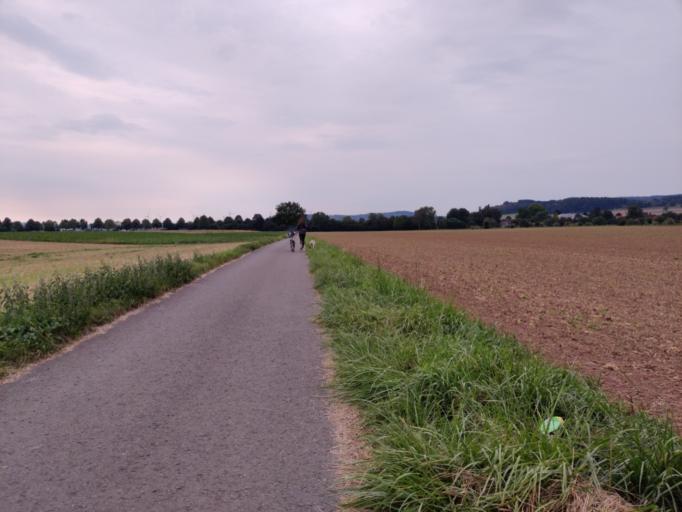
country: DE
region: Lower Saxony
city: Hameln
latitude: 52.0691
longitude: 9.3569
